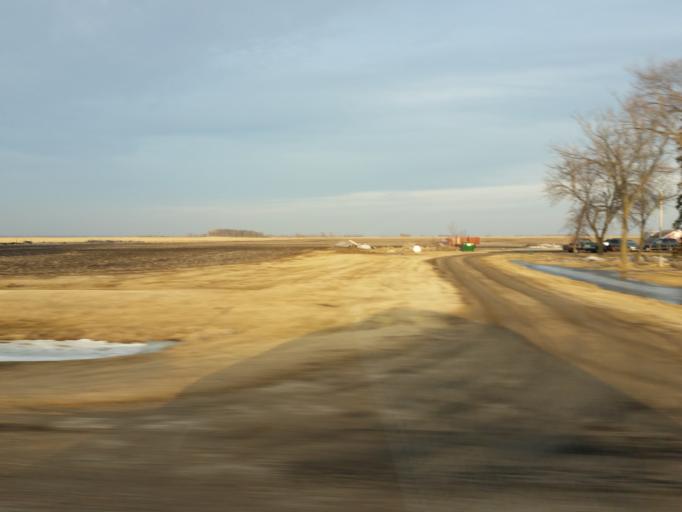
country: US
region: North Dakota
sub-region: Traill County
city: Mayville
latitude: 47.3882
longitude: -97.3263
